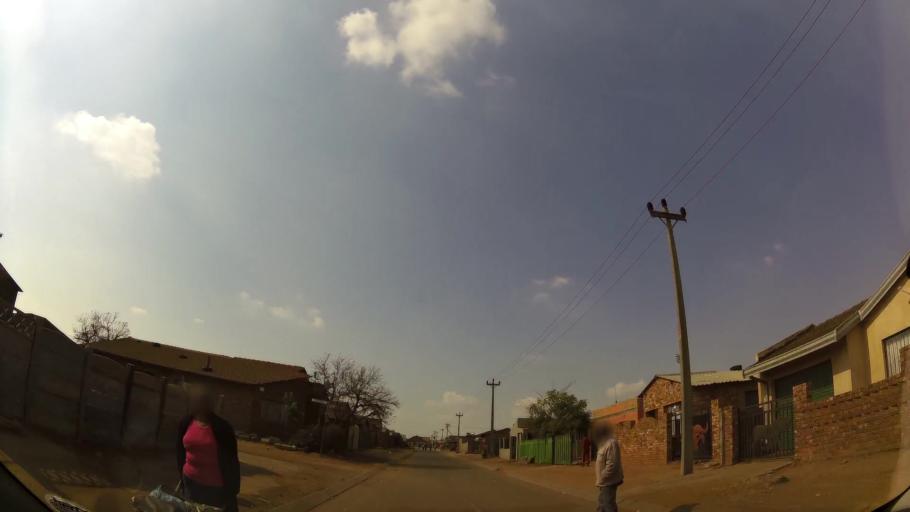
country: ZA
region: Gauteng
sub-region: Ekurhuleni Metropolitan Municipality
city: Springs
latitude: -26.1183
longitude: 28.4812
